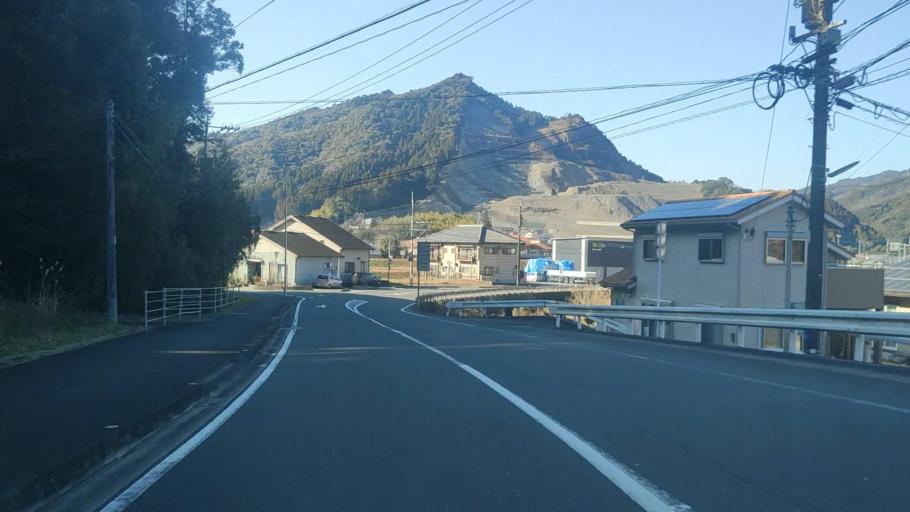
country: JP
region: Oita
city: Saiki
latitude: 32.9768
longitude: 131.8527
